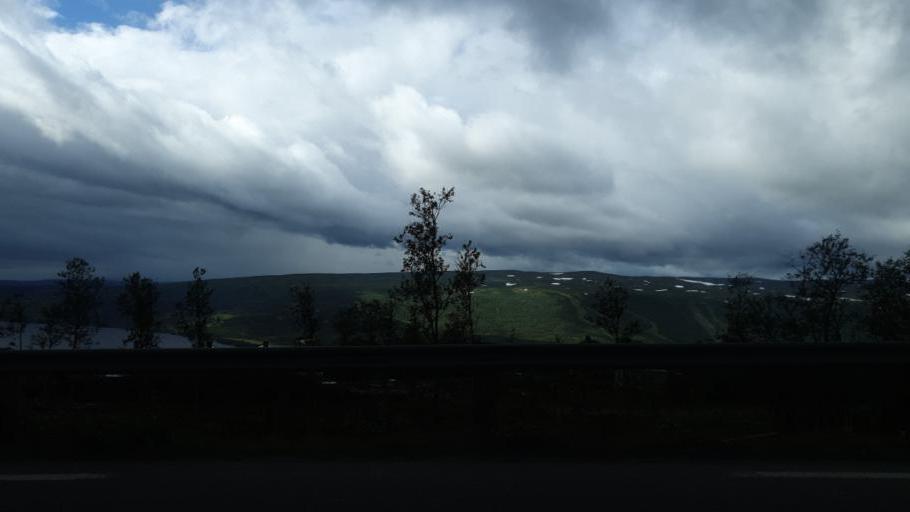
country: NO
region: Oppland
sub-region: Vestre Slidre
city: Slidre
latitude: 61.2511
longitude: 8.8832
